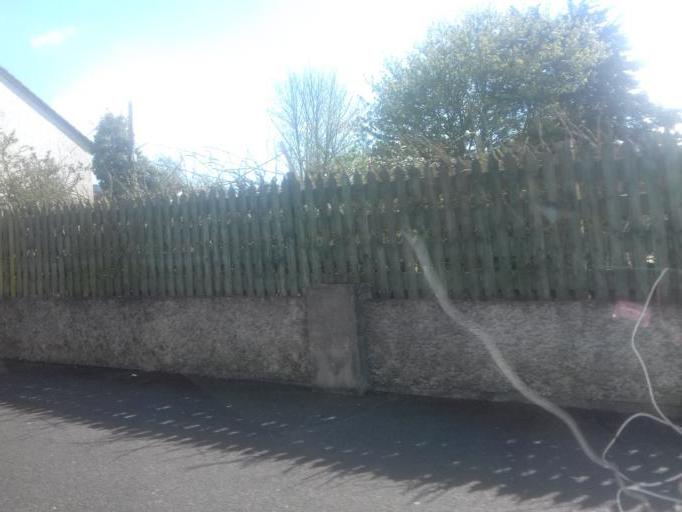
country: IE
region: Leinster
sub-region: Laois
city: Portlaoise
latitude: 53.0382
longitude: -7.2943
